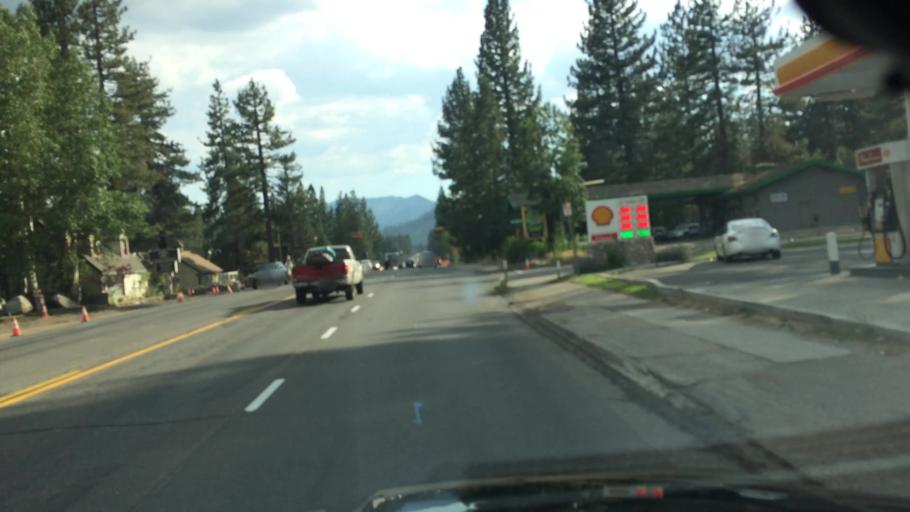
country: US
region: California
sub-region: El Dorado County
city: South Lake Tahoe
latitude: 38.9250
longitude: -119.9869
